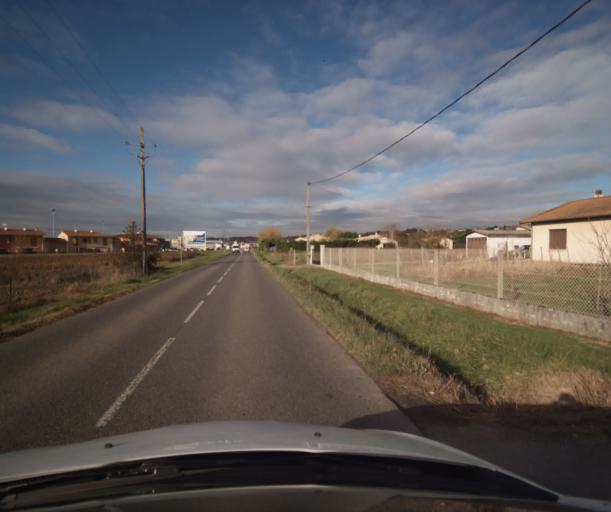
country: FR
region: Midi-Pyrenees
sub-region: Departement de la Haute-Garonne
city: Bruguieres
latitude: 43.7180
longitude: 1.4167
